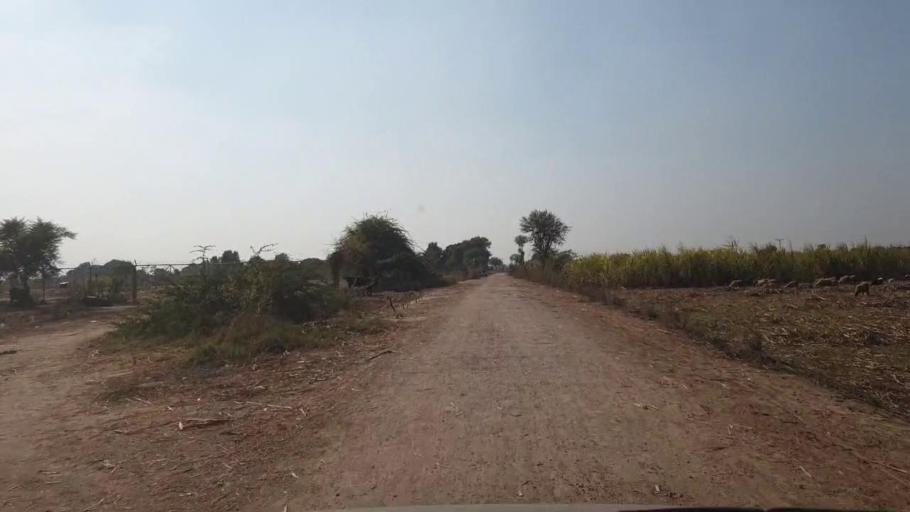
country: PK
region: Sindh
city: Chambar
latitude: 25.3306
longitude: 68.7670
